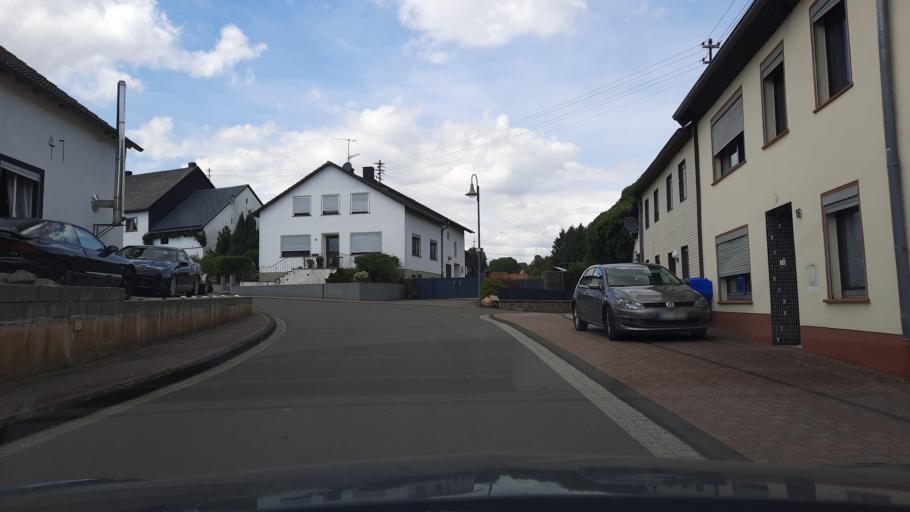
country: DE
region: Rheinland-Pfalz
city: Watzerath
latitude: 50.1919
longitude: 6.3706
